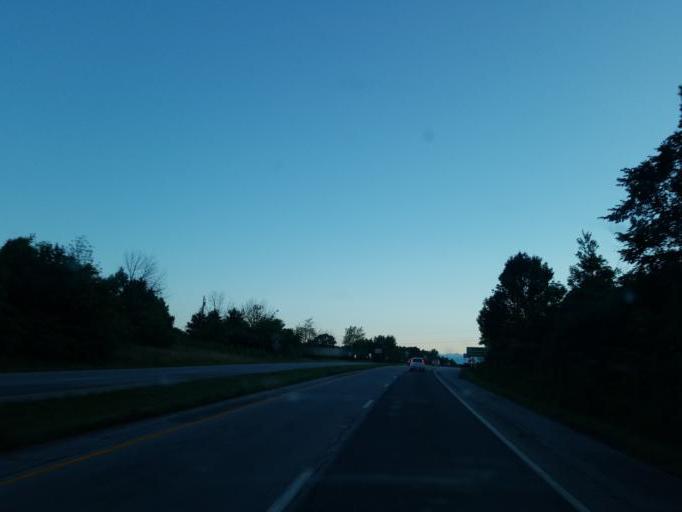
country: US
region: Ohio
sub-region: Summit County
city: Clinton
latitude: 40.9405
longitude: -81.6573
